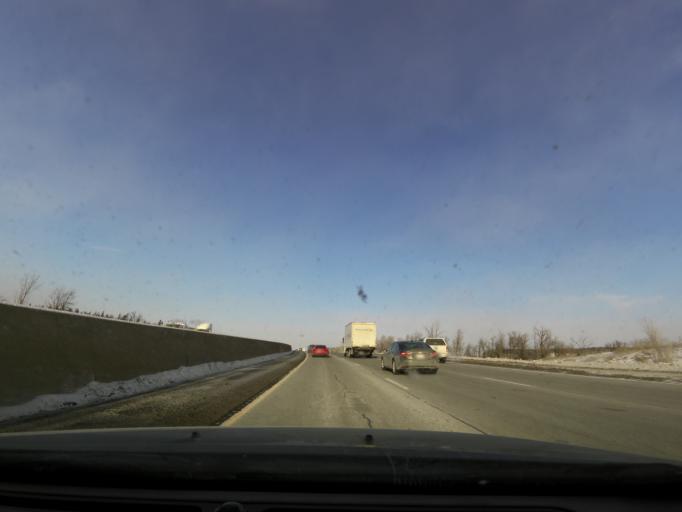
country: CA
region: Ontario
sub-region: Halton
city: Milton
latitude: 43.4988
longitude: -79.9606
